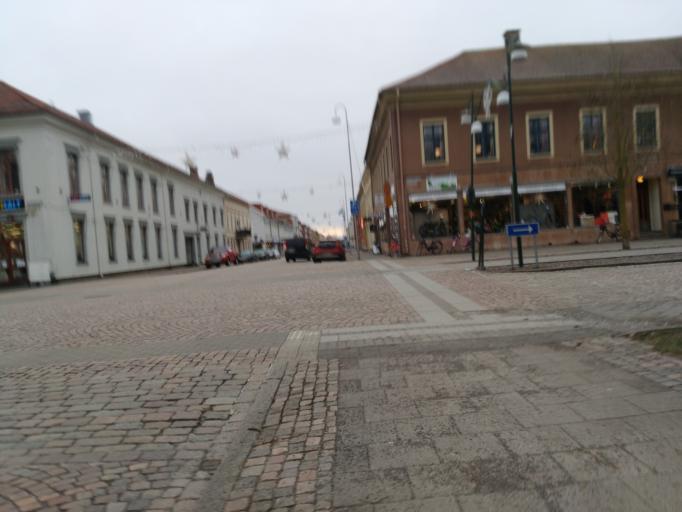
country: SE
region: Vaestra Goetaland
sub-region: Lidkopings Kommun
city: Lidkoping
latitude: 58.5027
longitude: 13.1617
